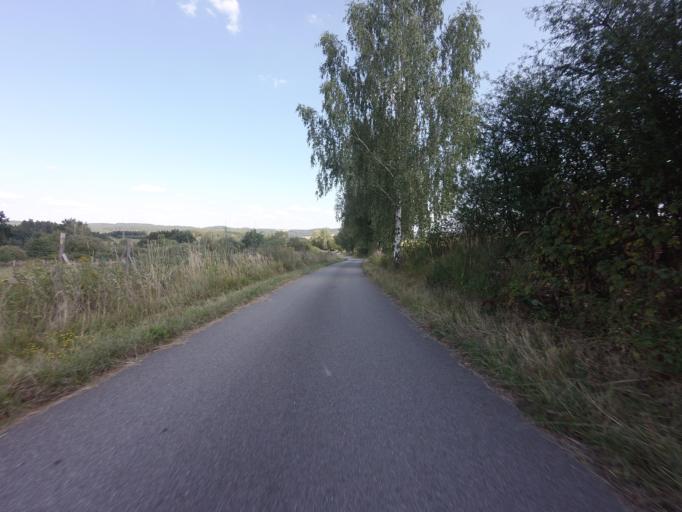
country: CZ
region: Jihocesky
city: Tyn nad Vltavou
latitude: 49.1739
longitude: 14.4291
